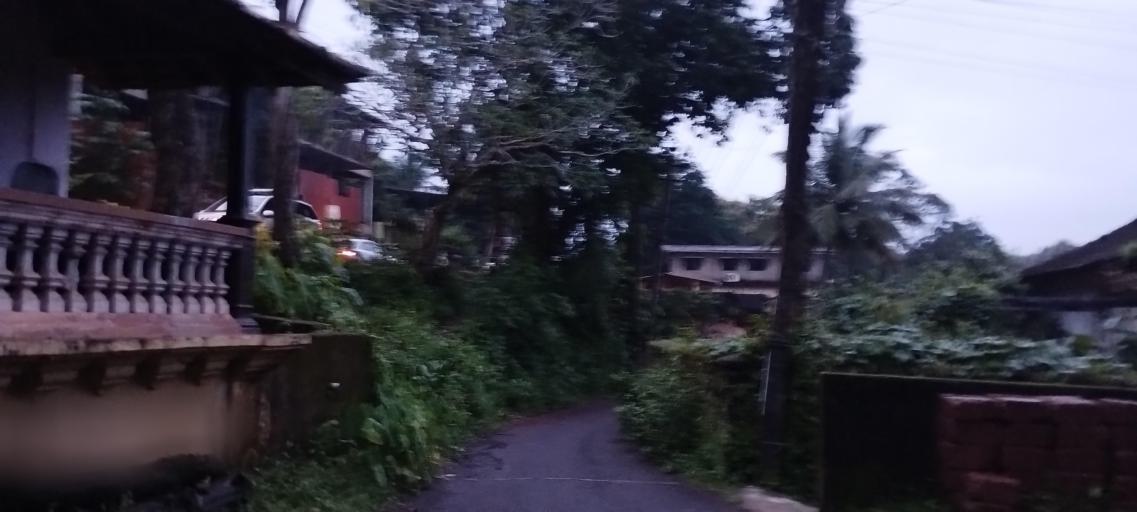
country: IN
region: Goa
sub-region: North Goa
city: Solim
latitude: 15.5995
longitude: 73.7776
